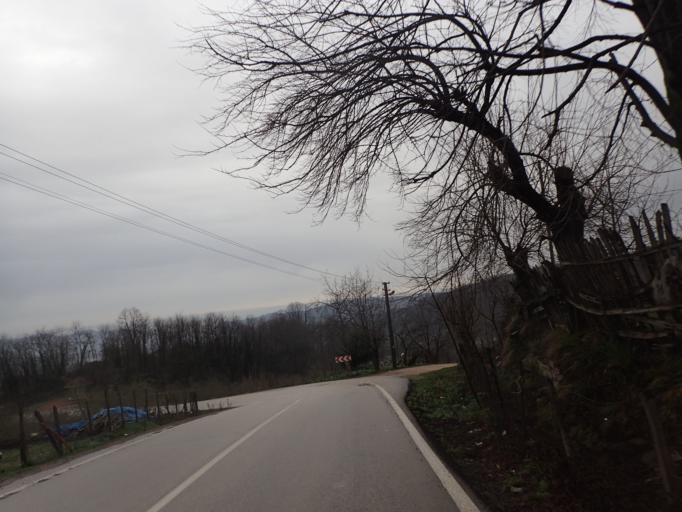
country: TR
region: Ordu
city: Camas
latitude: 40.9282
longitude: 37.5065
